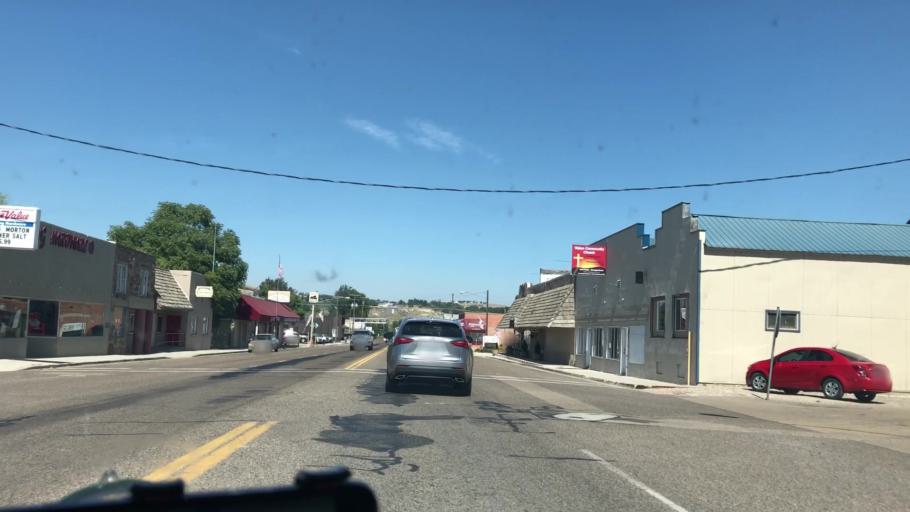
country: US
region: Idaho
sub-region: Owyhee County
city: Marsing
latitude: 43.5455
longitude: -116.8068
